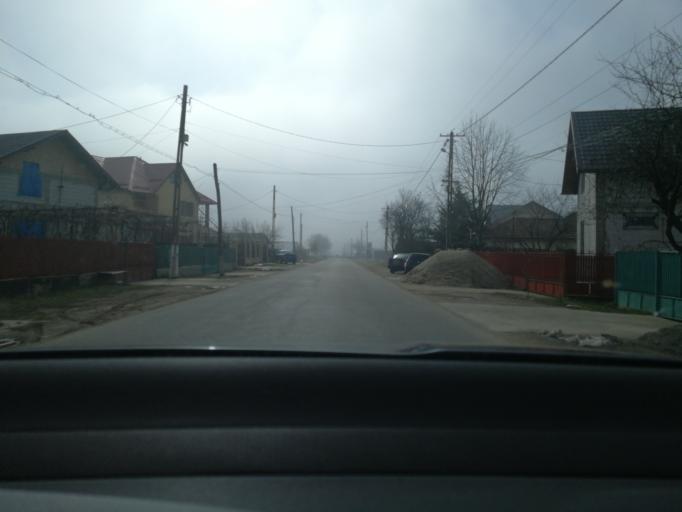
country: RO
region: Prahova
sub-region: Comuna Magureni
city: Lunca Prahovei
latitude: 45.0324
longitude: 25.7656
